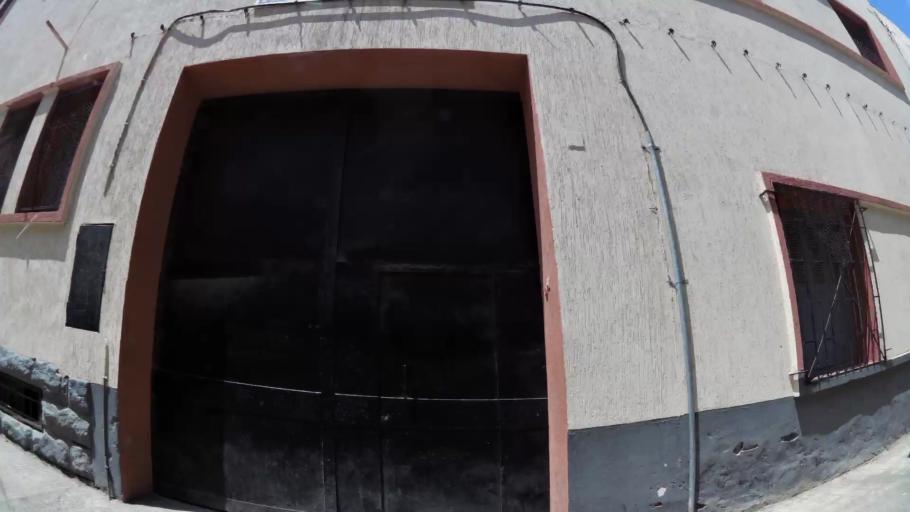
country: MA
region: Rabat-Sale-Zemmour-Zaer
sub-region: Rabat
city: Rabat
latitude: 34.0260
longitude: -6.8452
